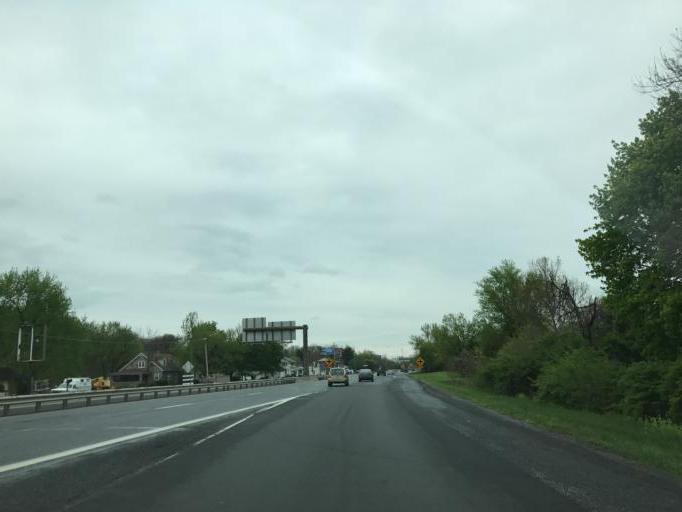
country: US
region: Pennsylvania
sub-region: Berks County
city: Blandon
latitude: 40.4344
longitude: -75.9101
